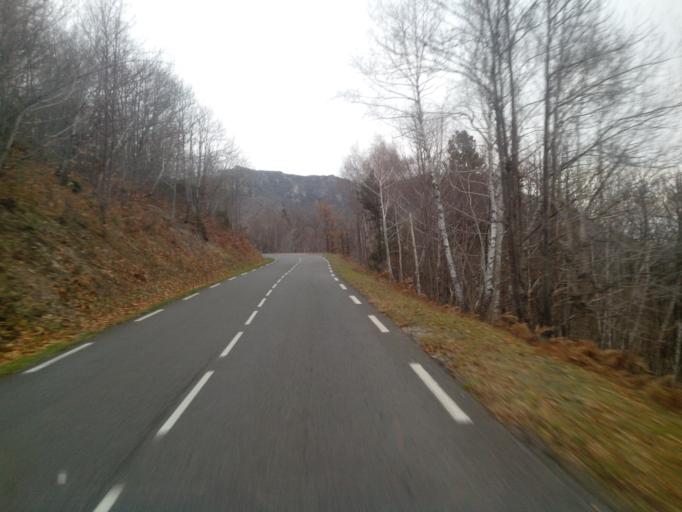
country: FR
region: Languedoc-Roussillon
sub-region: Departement de la Lozere
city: Florac
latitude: 44.2782
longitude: 3.5979
